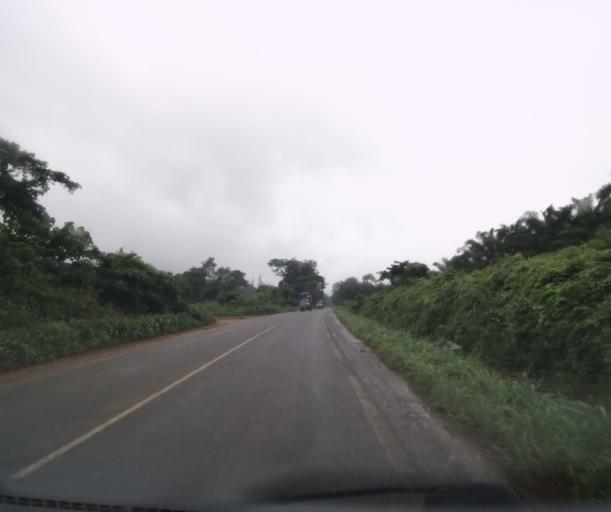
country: CM
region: Centre
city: Eseka
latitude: 3.8902
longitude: 10.7325
